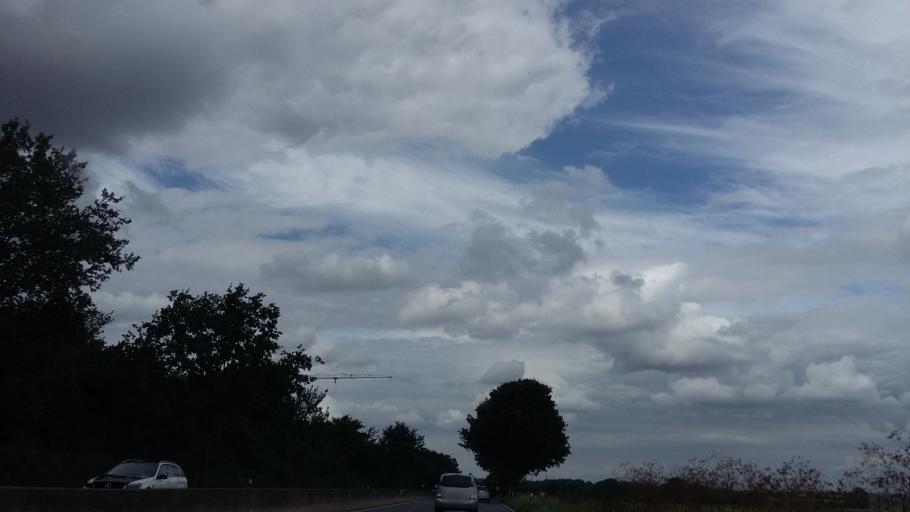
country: DE
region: Lower Saxony
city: Sarstedt
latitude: 52.2834
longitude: 9.8402
